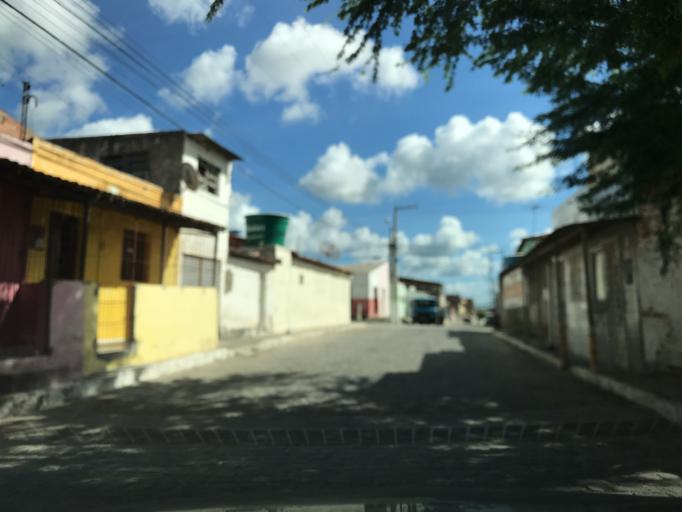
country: BR
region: Pernambuco
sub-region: Bezerros
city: Bezerros
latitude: -8.2341
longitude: -35.7450
